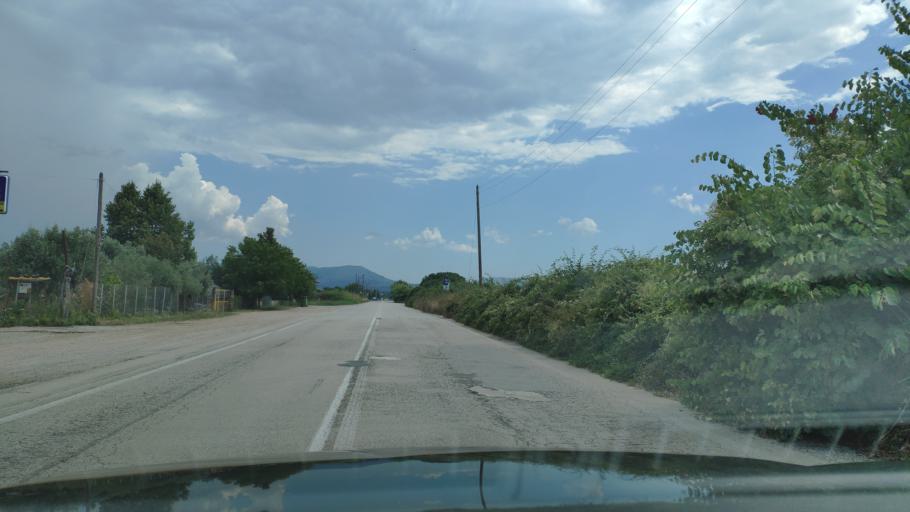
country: GR
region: West Greece
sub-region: Nomos Aitolias kai Akarnanias
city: Krikellos
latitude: 38.9531
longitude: 21.1759
